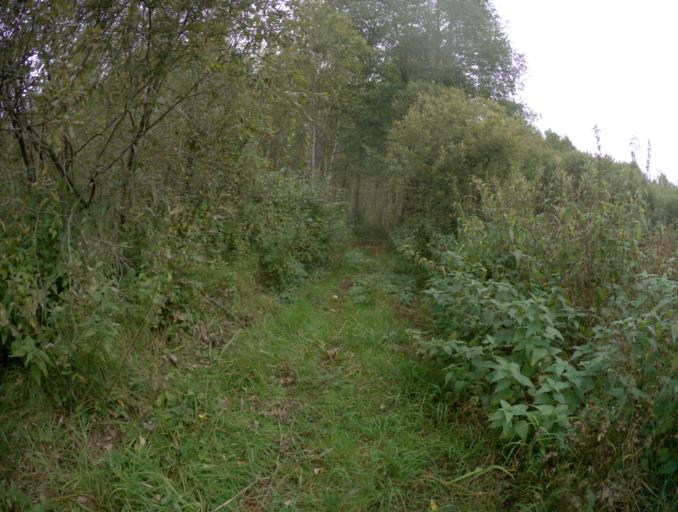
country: RU
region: Moskovskaya
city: Misheronskiy
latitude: 55.7753
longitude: 39.6046
